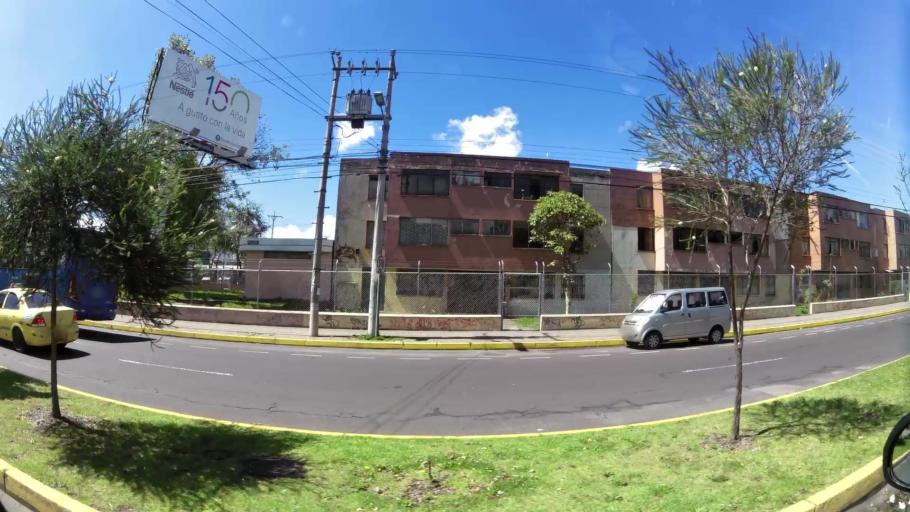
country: EC
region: Pichincha
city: Quito
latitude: -0.2646
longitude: -78.5402
